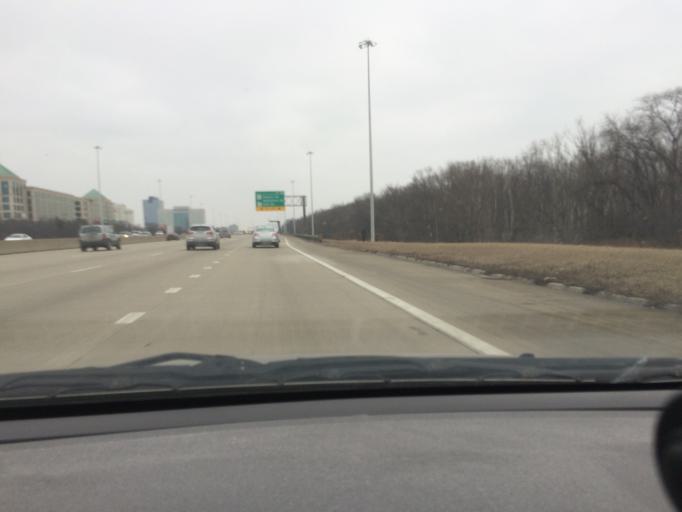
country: US
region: Illinois
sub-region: Cook County
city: Hoffman Estates
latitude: 42.0227
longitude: -88.0309
